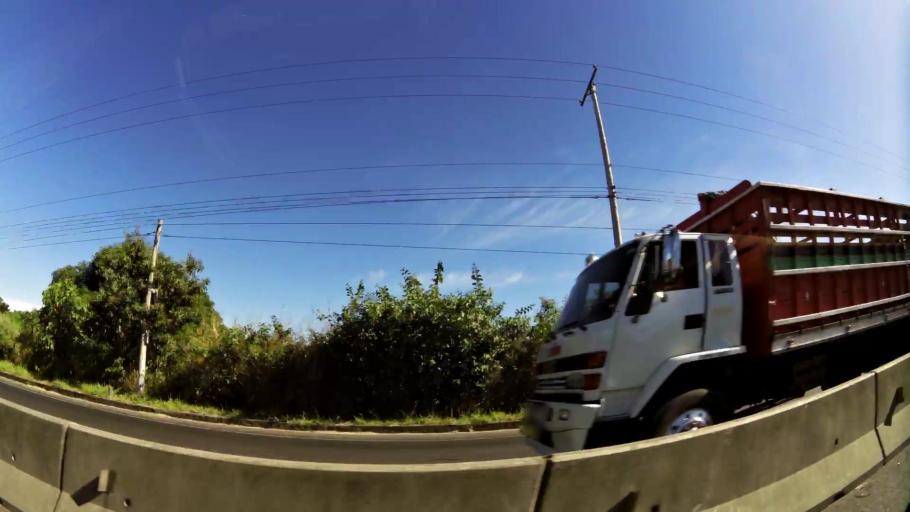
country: SV
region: Santa Ana
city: Coatepeque
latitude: 13.9422
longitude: -89.5472
